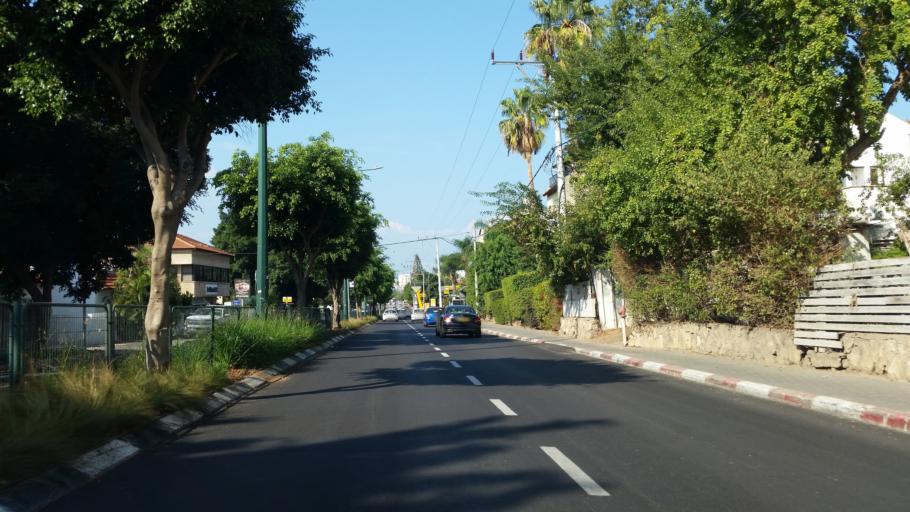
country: IL
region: Tel Aviv
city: Herzliyya
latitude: 32.1628
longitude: 34.8319
